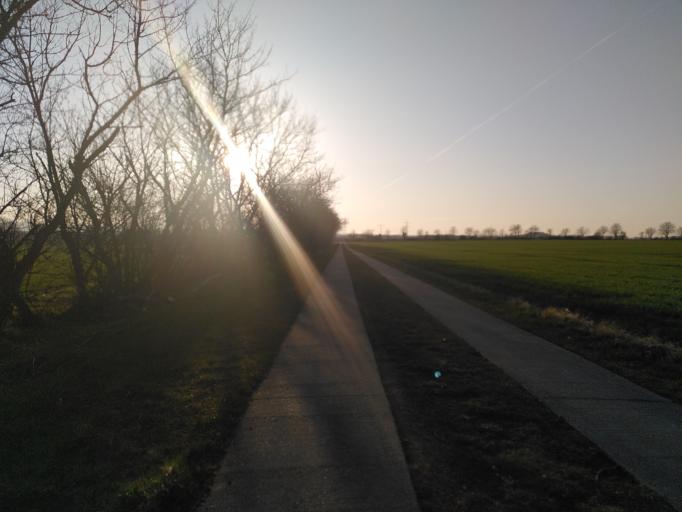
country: DE
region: Saxony-Anhalt
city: Ditfurt
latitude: 51.7962
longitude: 11.2094
